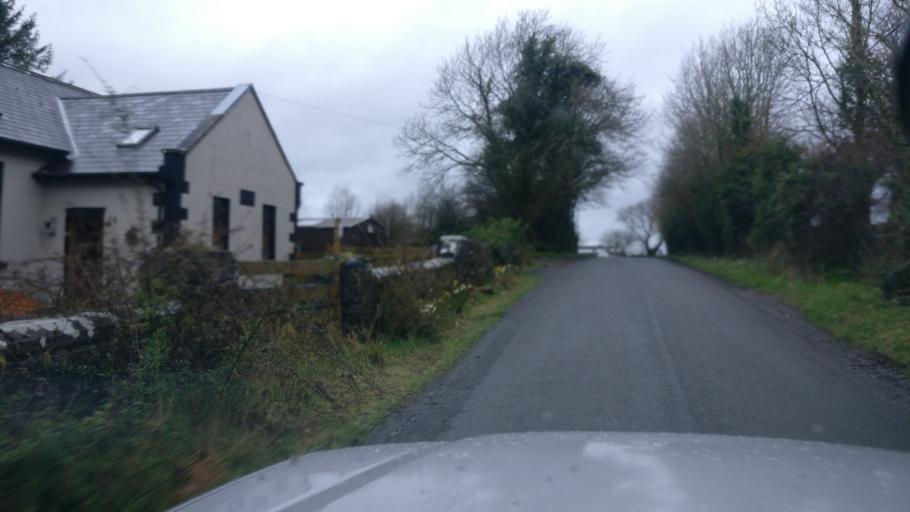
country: IE
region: Connaught
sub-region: County Galway
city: Ballinasloe
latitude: 53.2618
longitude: -8.3562
